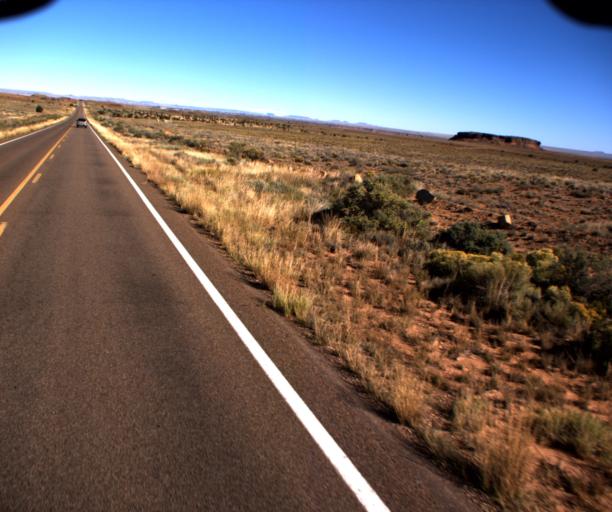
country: US
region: Arizona
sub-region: Navajo County
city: Holbrook
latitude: 34.8286
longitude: -110.1429
